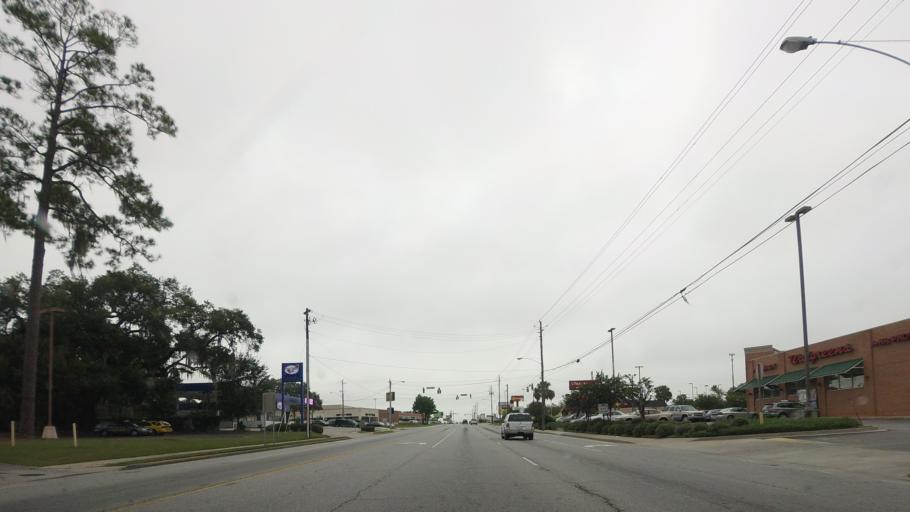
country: US
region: Georgia
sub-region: Lowndes County
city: Remerton
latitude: 30.8687
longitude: -83.2875
